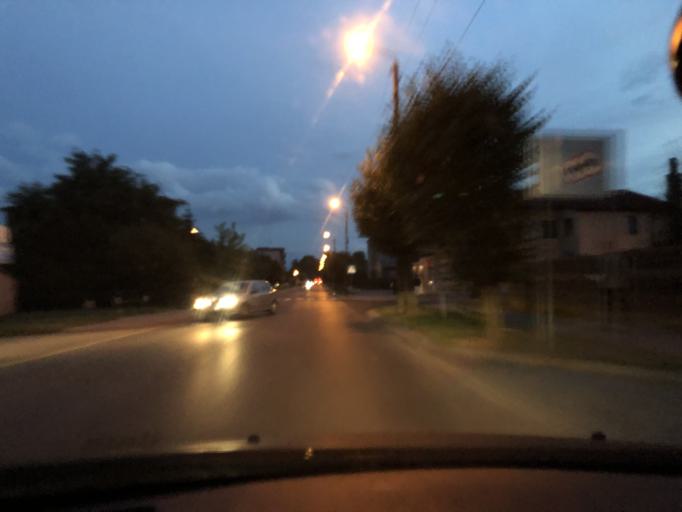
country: PL
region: Lodz Voivodeship
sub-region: Powiat wielunski
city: Wielun
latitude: 51.2246
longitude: 18.5584
